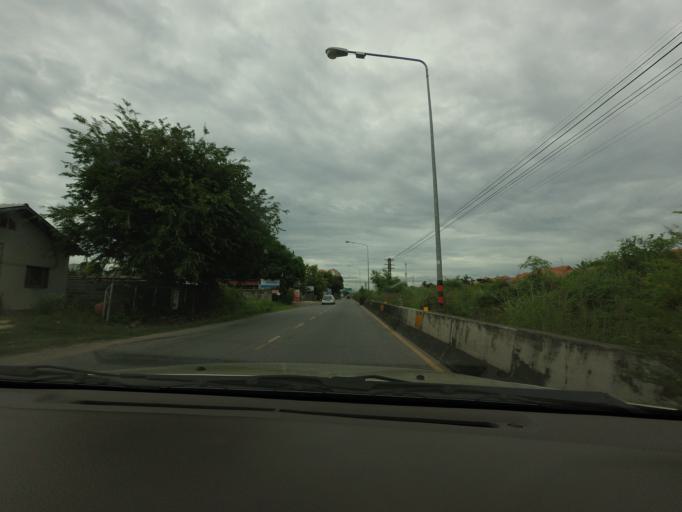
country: TH
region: Chon Buri
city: Phatthaya
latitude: 12.9057
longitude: 100.9008
